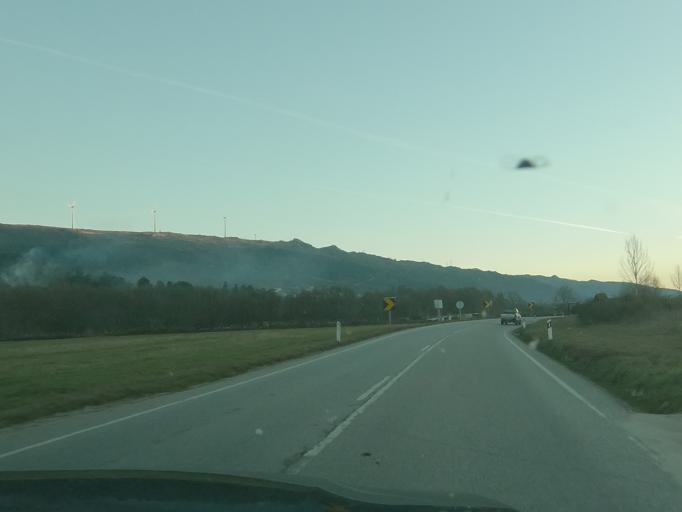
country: PT
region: Vila Real
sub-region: Vila Pouca de Aguiar
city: Vila Pouca de Aguiar
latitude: 41.4600
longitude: -7.6651
